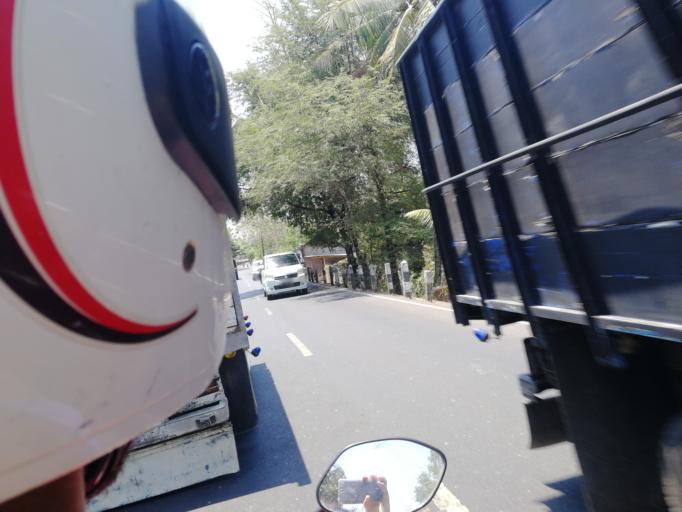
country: ID
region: Bali
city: Banjar Trunyan
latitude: -8.1458
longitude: 115.4004
